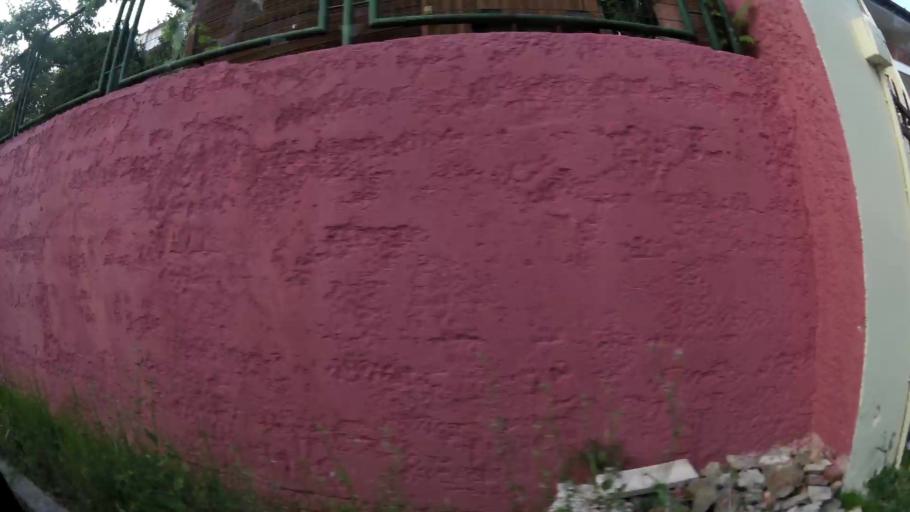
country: GR
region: Central Macedonia
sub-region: Nomos Thessalonikis
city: Pefka
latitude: 40.6602
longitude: 23.0011
